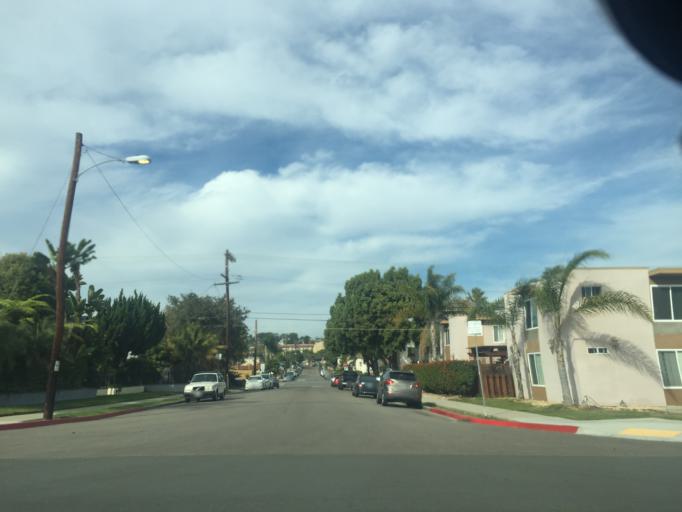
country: US
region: California
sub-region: San Diego County
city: La Jolla
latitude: 32.7977
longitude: -117.2363
